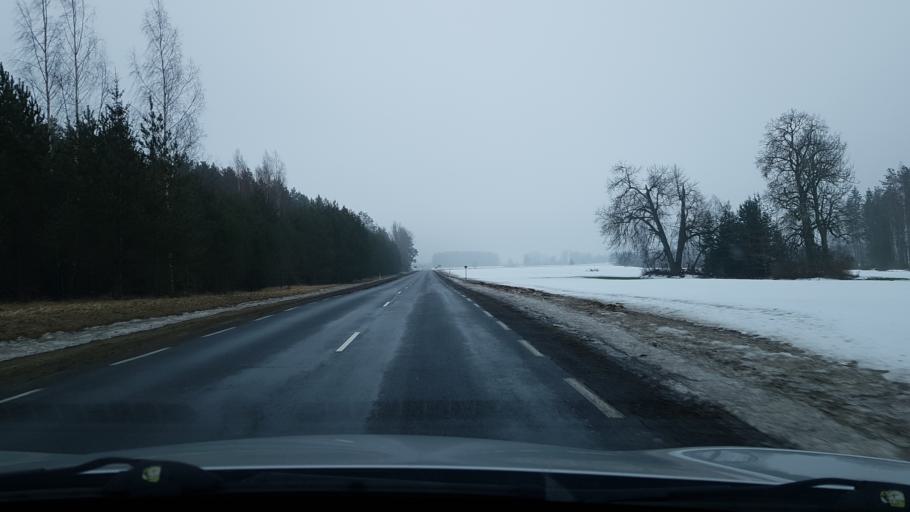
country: EE
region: Valgamaa
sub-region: Torva linn
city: Torva
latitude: 58.1156
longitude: 25.9982
